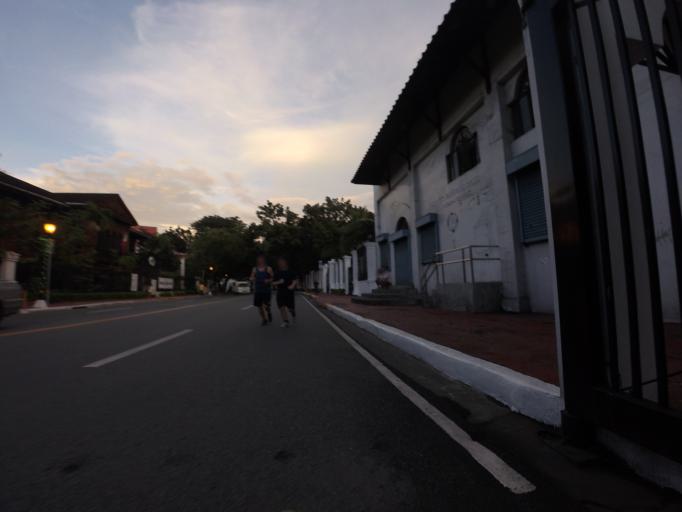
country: PH
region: Metro Manila
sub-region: City of Manila
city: Quiapo
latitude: 14.5926
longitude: 120.9919
